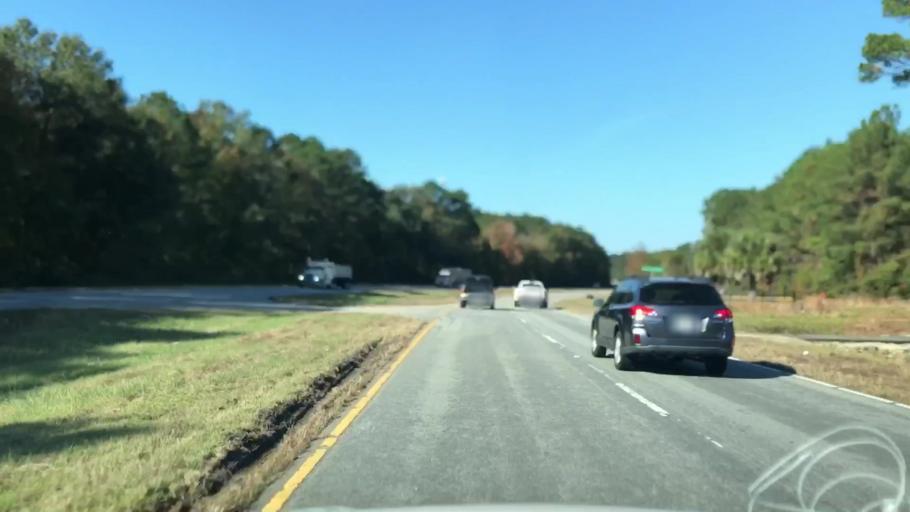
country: US
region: South Carolina
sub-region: Charleston County
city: Ravenel
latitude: 32.7582
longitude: -80.3821
